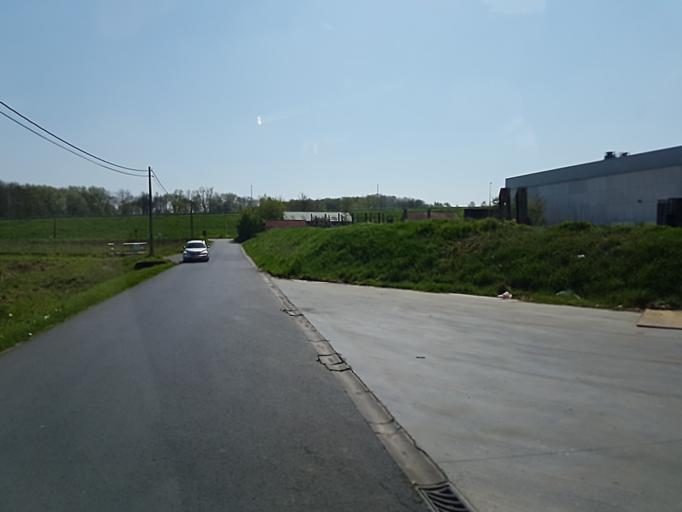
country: BE
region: Flanders
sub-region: Provincie West-Vlaanderen
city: Zonnebeke
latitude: 50.8401
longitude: 3.0054
